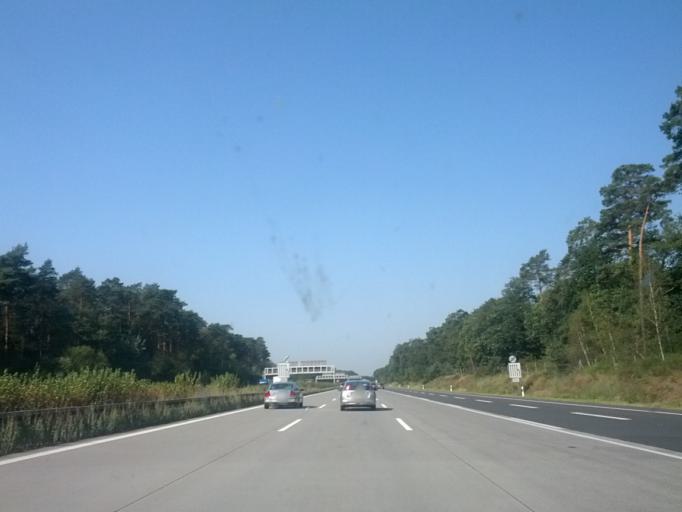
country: DE
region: Brandenburg
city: Mittenwalde
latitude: 52.3189
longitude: 13.5469
